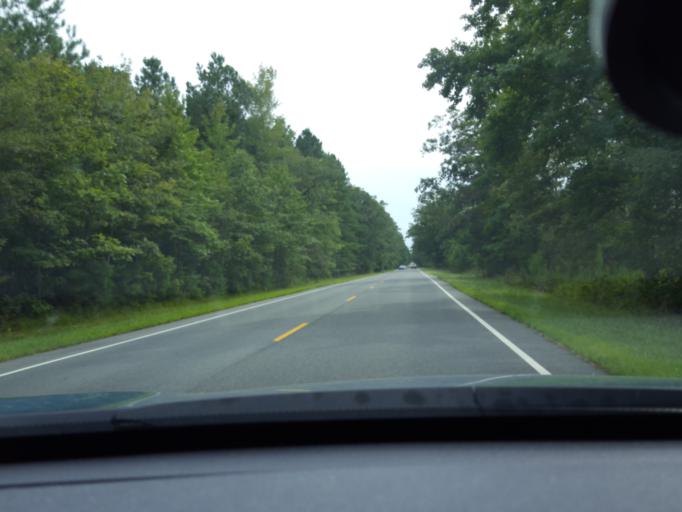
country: US
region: Virginia
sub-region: Caroline County
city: Bowling Green
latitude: 37.9826
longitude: -77.3390
